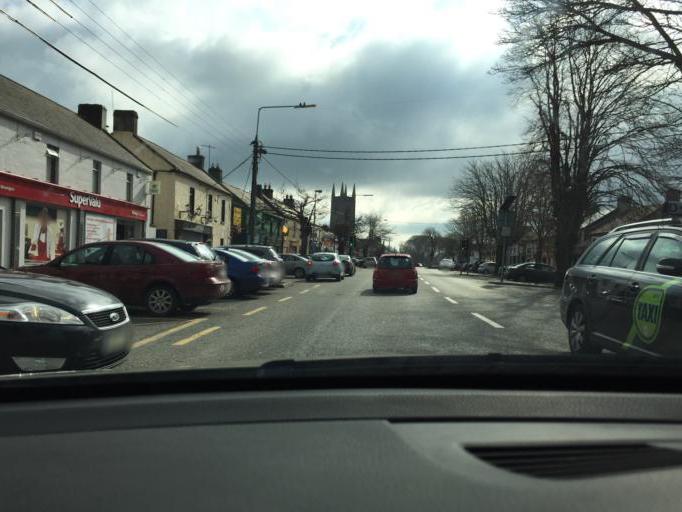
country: IE
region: Leinster
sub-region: Wicklow
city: Blessington
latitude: 53.1723
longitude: -6.5305
